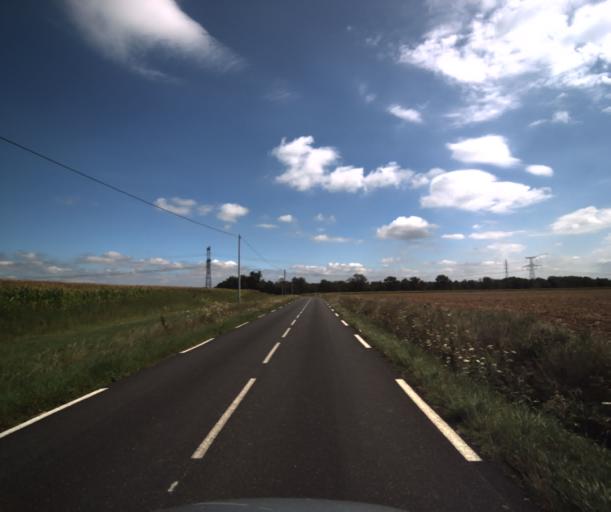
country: FR
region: Midi-Pyrenees
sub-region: Departement de la Haute-Garonne
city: Longages
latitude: 43.3785
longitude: 1.2435
